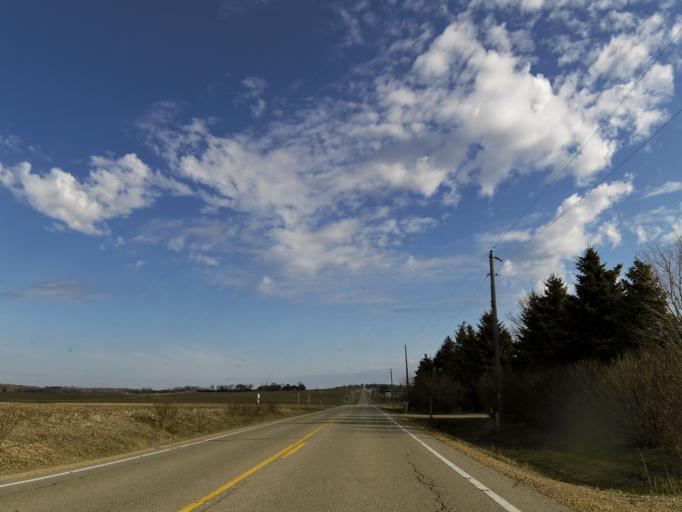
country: US
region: Minnesota
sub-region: Washington County
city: Cottage Grove
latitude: 44.8359
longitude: -92.8628
